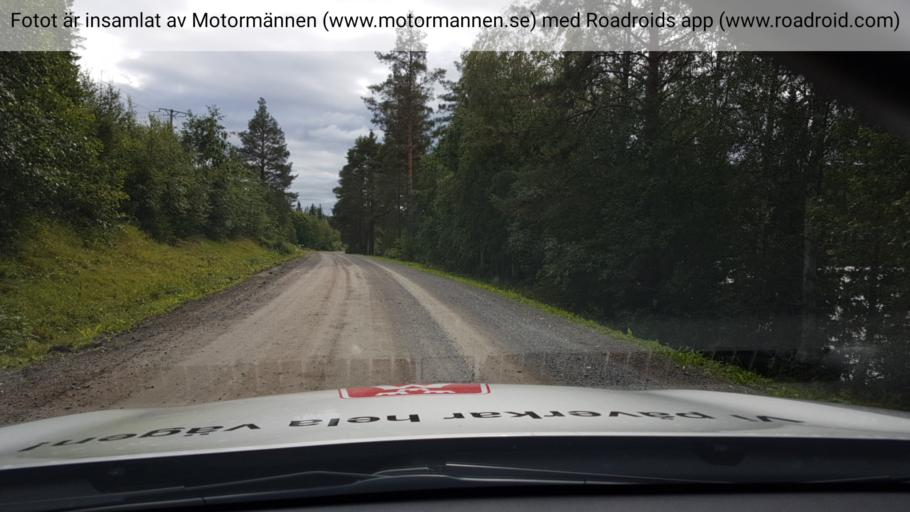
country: SE
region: Jaemtland
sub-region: Ragunda Kommun
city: Hammarstrand
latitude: 62.9543
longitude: 16.1149
